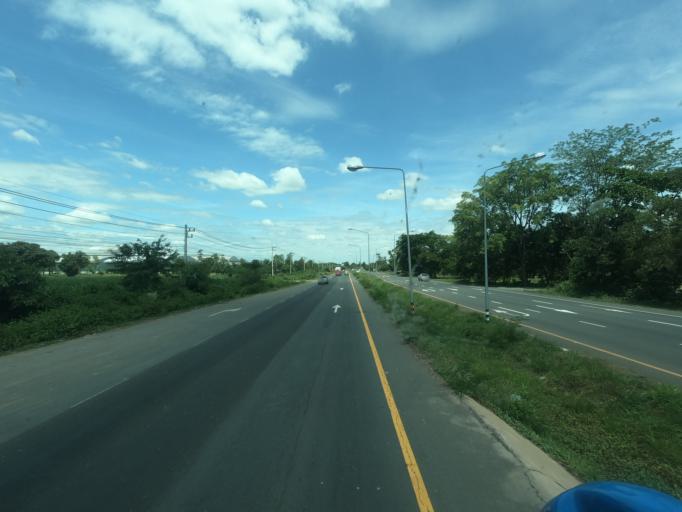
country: TH
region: Surin
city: Prasat
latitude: 14.6115
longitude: 103.3361
